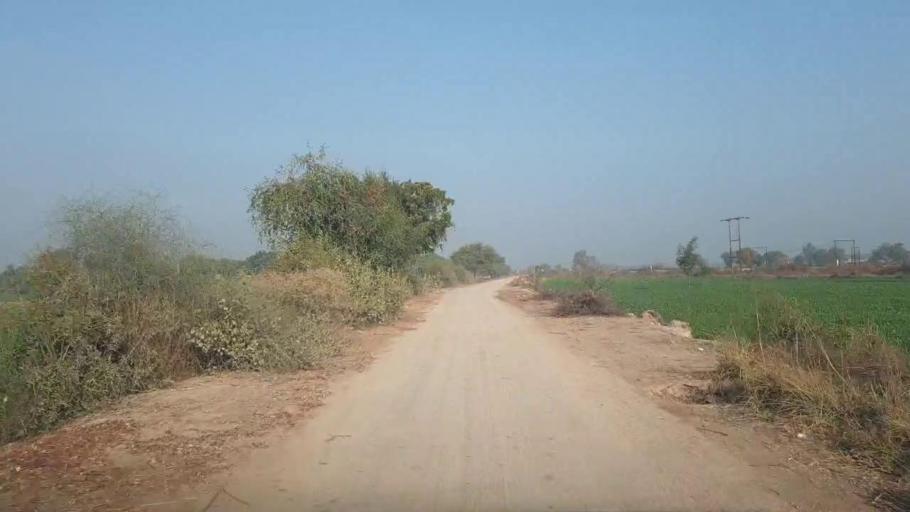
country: PK
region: Sindh
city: Shahdadpur
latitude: 25.9608
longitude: 68.6143
